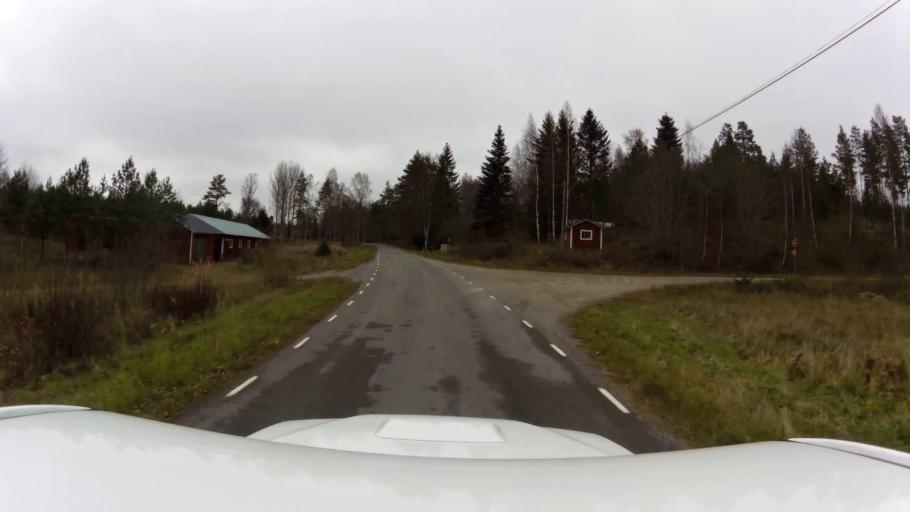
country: SE
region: OEstergoetland
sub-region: Kinda Kommun
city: Kisa
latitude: 58.1307
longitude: 15.4532
